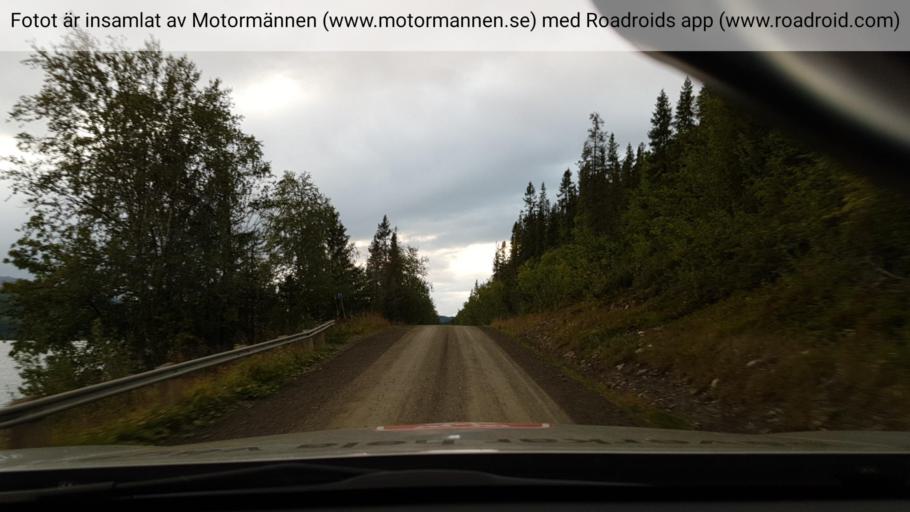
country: NO
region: Nordland
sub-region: Hattfjelldal
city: Hattfjelldal
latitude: 65.6347
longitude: 15.2185
